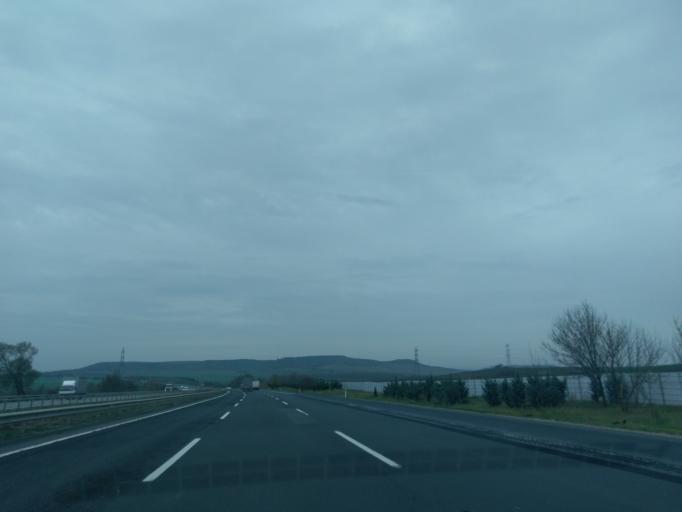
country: TR
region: Istanbul
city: Canta
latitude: 41.1484
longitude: 28.1462
